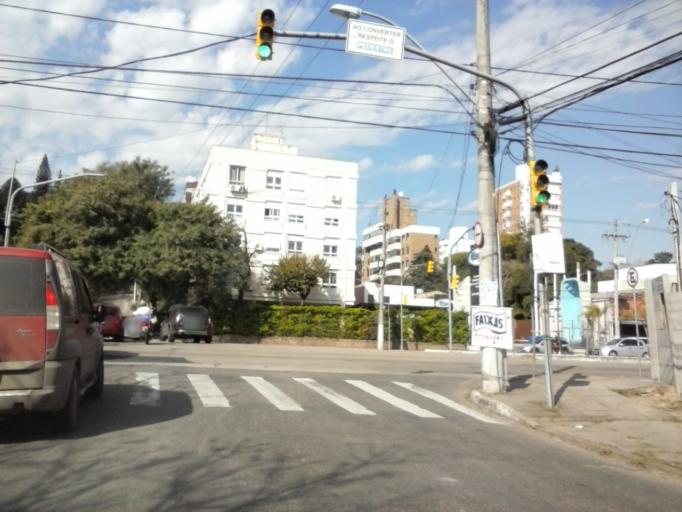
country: BR
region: Rio Grande do Sul
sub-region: Porto Alegre
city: Porto Alegre
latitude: -30.0518
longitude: -51.1814
